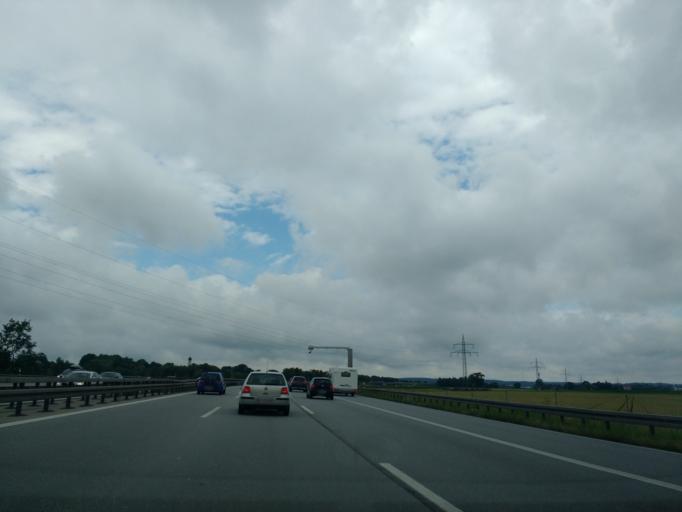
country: DE
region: Bavaria
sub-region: Upper Bavaria
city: Kranzberg
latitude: 48.3976
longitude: 11.5935
